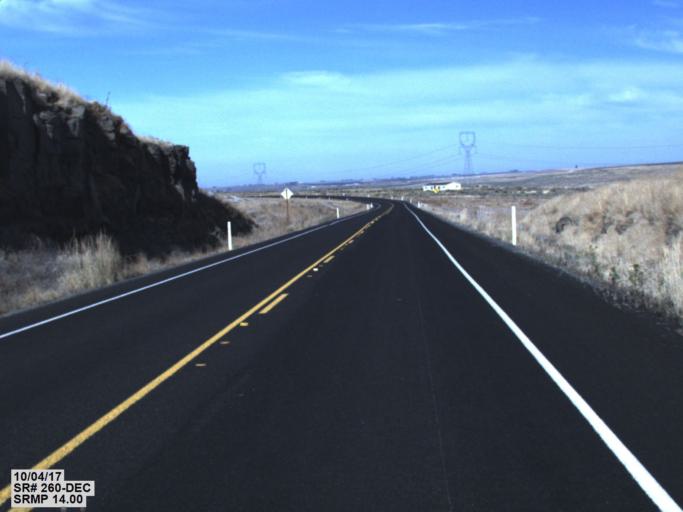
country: US
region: Washington
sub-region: Franklin County
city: Connell
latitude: 46.6327
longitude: -118.7574
